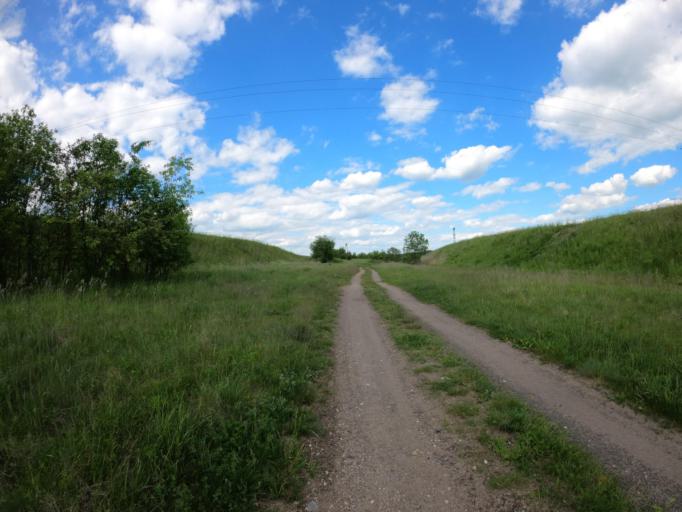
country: PL
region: Warmian-Masurian Voivodeship
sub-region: Powiat lidzbarski
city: Lidzbark Warminski
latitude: 54.1396
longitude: 20.6002
